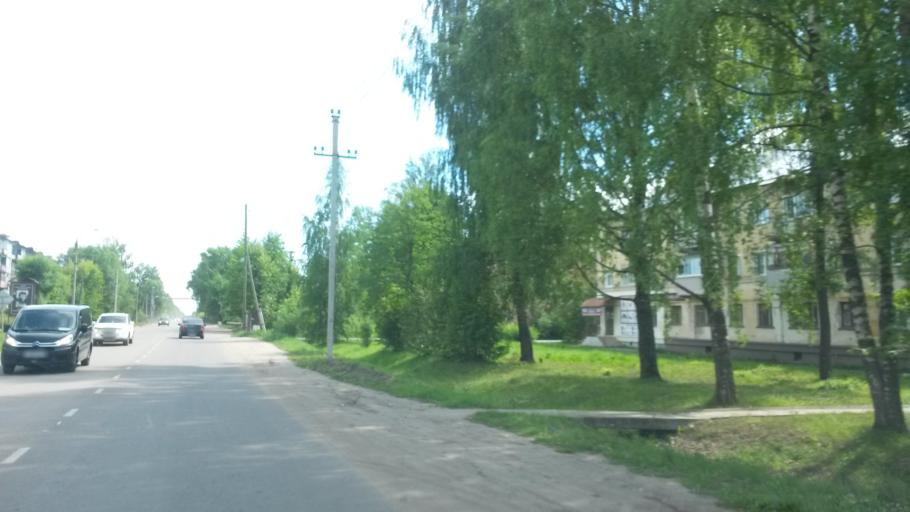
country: RU
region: Ivanovo
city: Zavolzhsk
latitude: 57.4941
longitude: 42.1349
